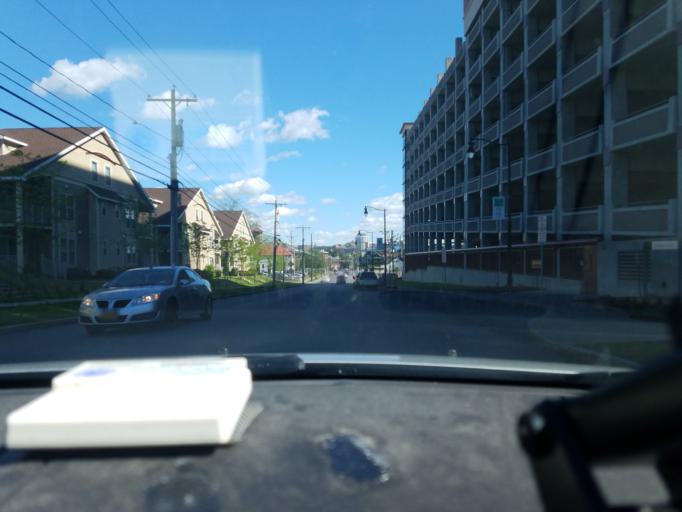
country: US
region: New York
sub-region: Onondaga County
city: Syracuse
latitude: 43.0562
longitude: -76.1482
